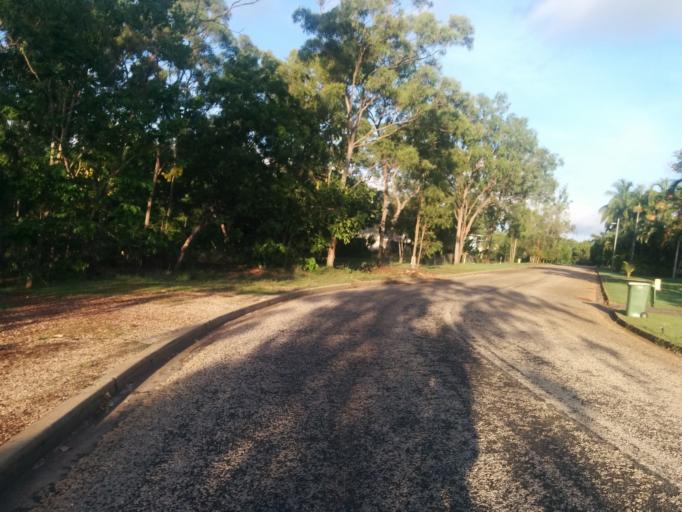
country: AU
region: Northern Territory
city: Alyangula
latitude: -13.8460
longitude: 136.4149
